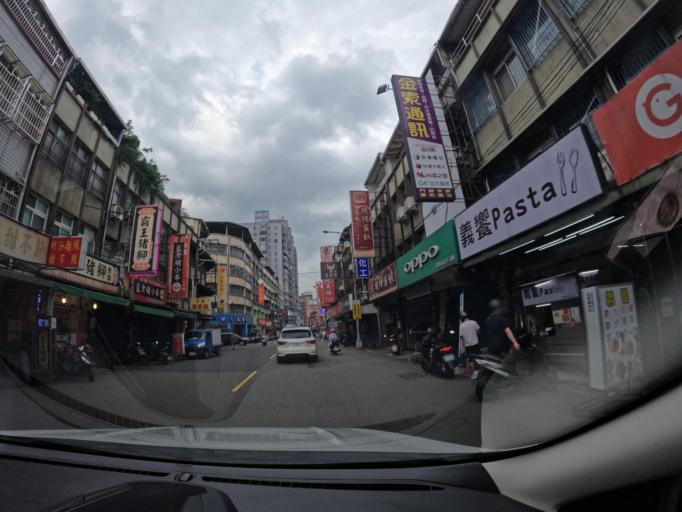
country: TW
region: Taiwan
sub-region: Taoyuan
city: Taoyuan
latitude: 24.9535
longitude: 121.3475
